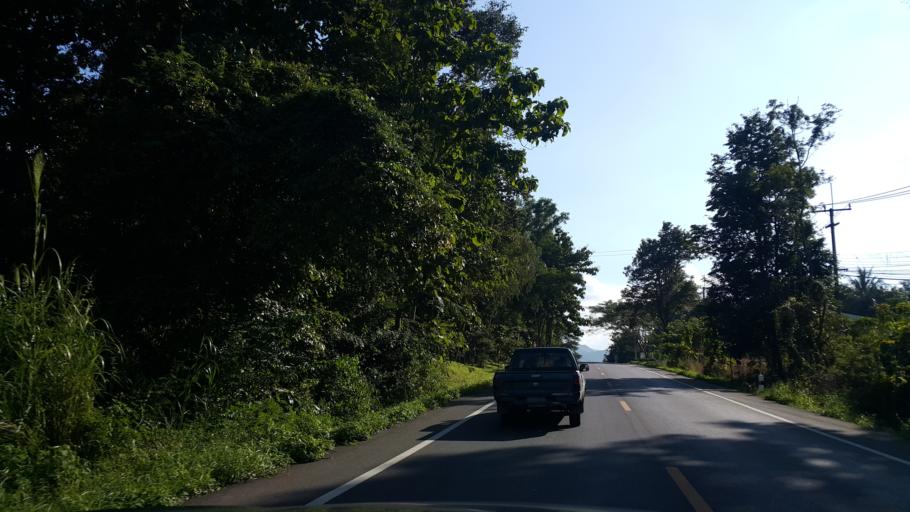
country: TH
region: Lamphun
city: Mae Tha
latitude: 18.5031
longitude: 99.2004
